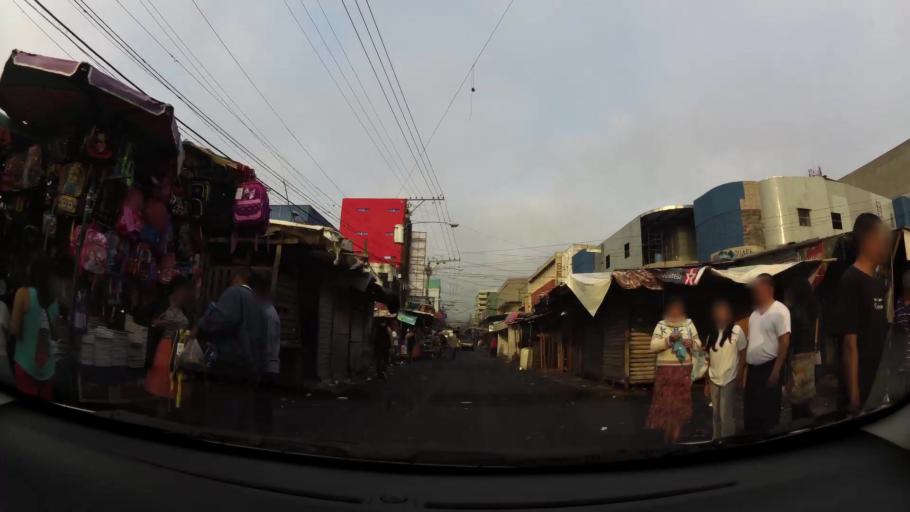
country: SV
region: San Salvador
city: San Salvador
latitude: 13.6974
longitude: -89.1936
